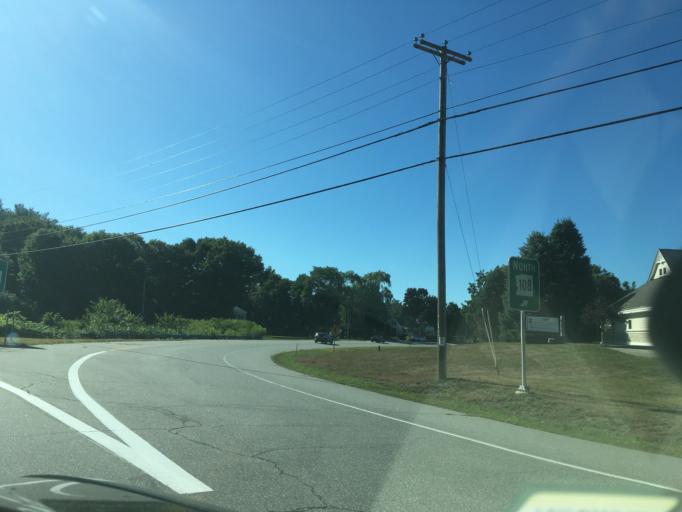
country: US
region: New Hampshire
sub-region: Rockingham County
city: Stratham Station
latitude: 43.0237
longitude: -70.9163
